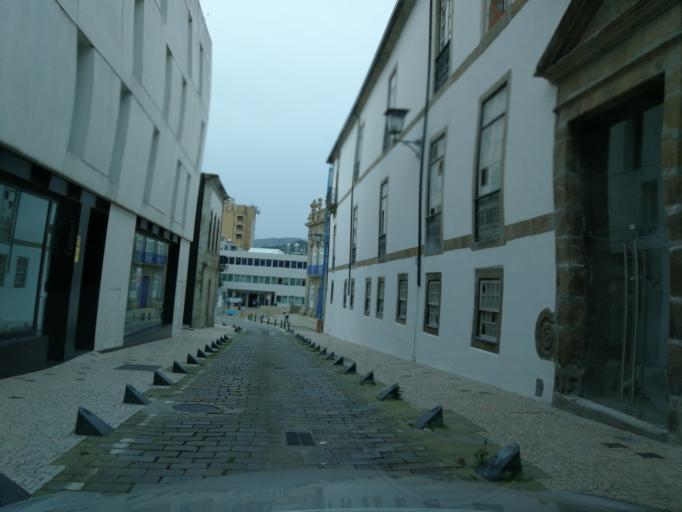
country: PT
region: Braga
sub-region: Braga
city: Braga
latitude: 41.5489
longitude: -8.4229
